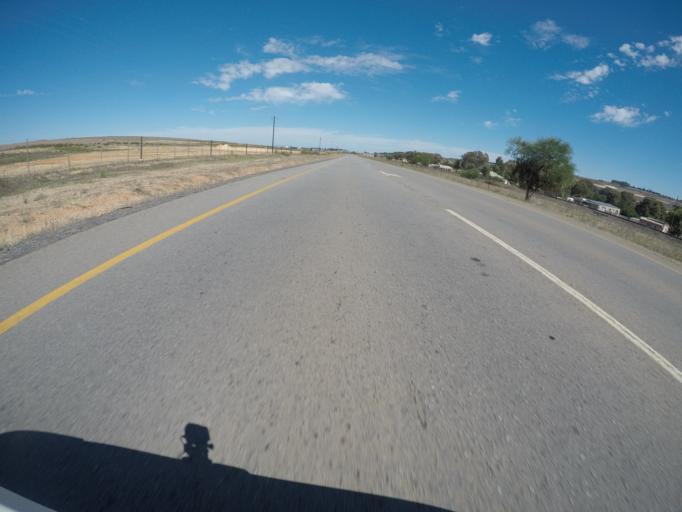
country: ZA
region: Western Cape
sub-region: West Coast District Municipality
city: Malmesbury
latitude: -33.4890
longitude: 18.6859
